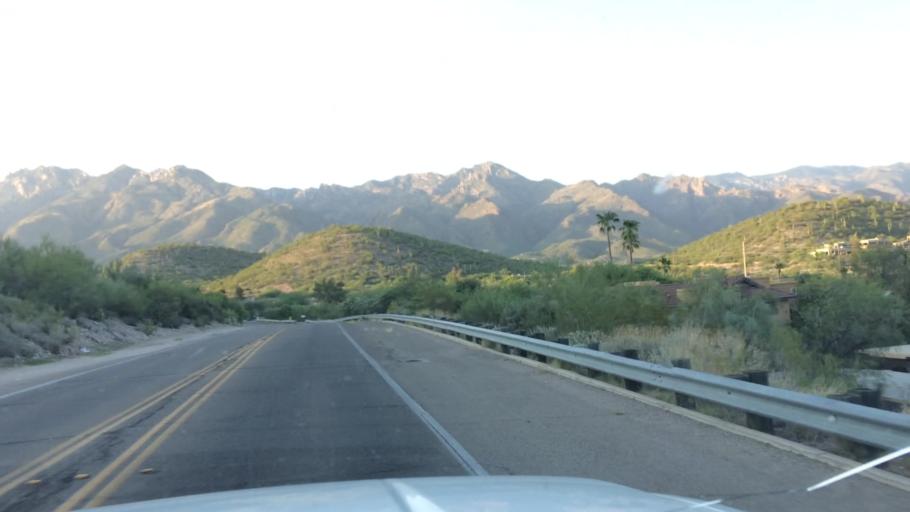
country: US
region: Arizona
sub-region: Pima County
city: Catalina Foothills
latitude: 32.2957
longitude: -110.8396
